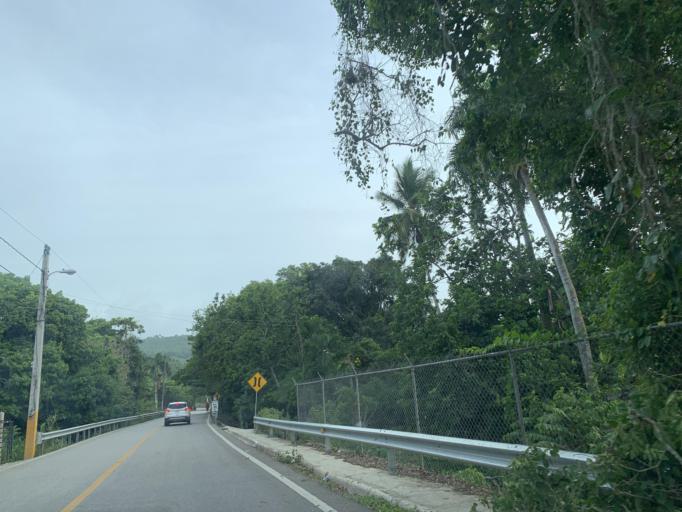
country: DO
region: Santiago
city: Pedro Garcia
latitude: 19.6995
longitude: -70.6238
